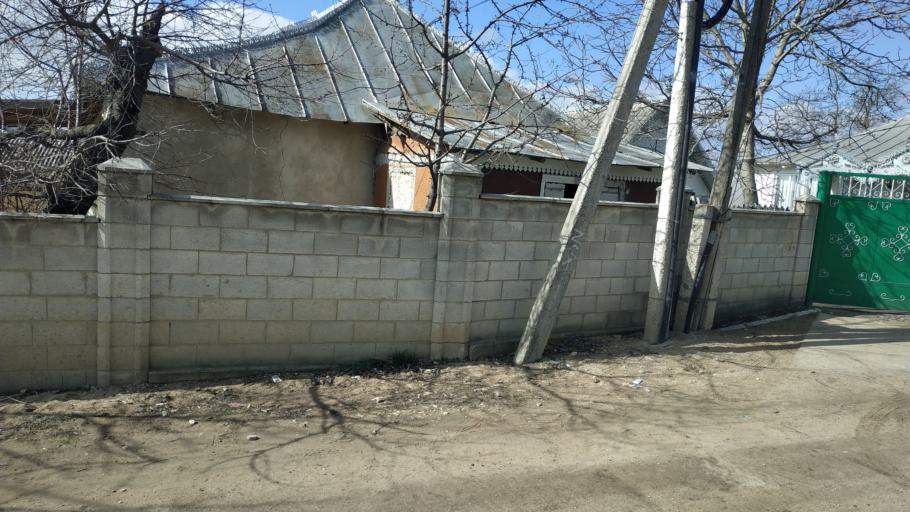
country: MD
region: Straseni
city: Straseni
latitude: 47.0223
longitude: 28.5482
